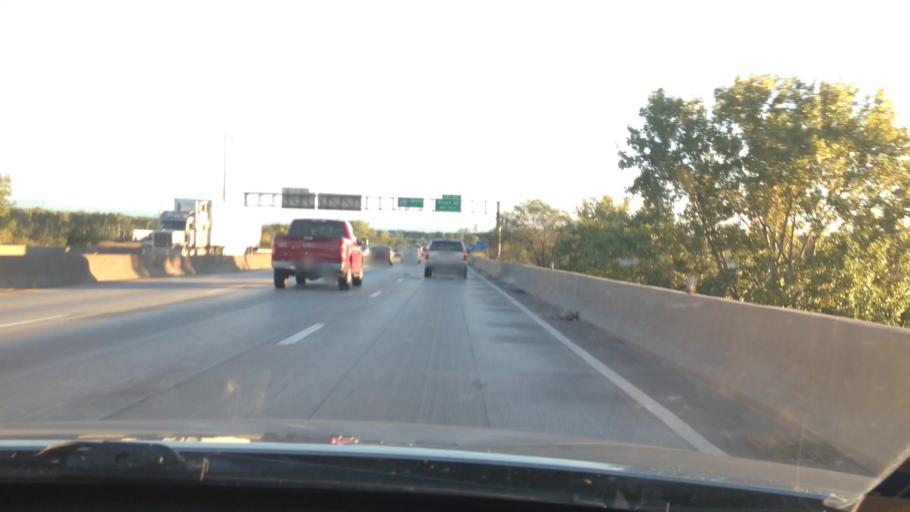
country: US
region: Missouri
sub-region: Clay County
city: Claycomo
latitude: 39.1460
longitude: -94.4986
